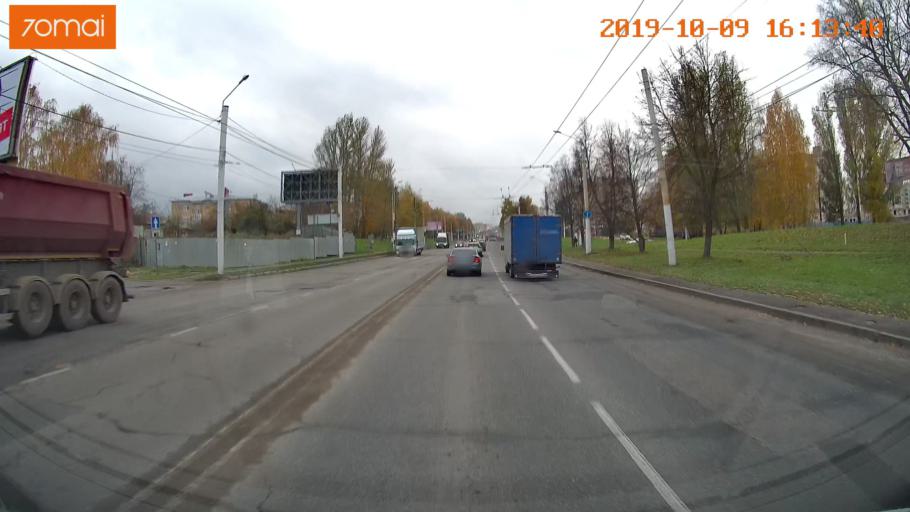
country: RU
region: Kostroma
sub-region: Kostromskoy Rayon
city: Kostroma
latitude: 57.7457
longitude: 40.9282
